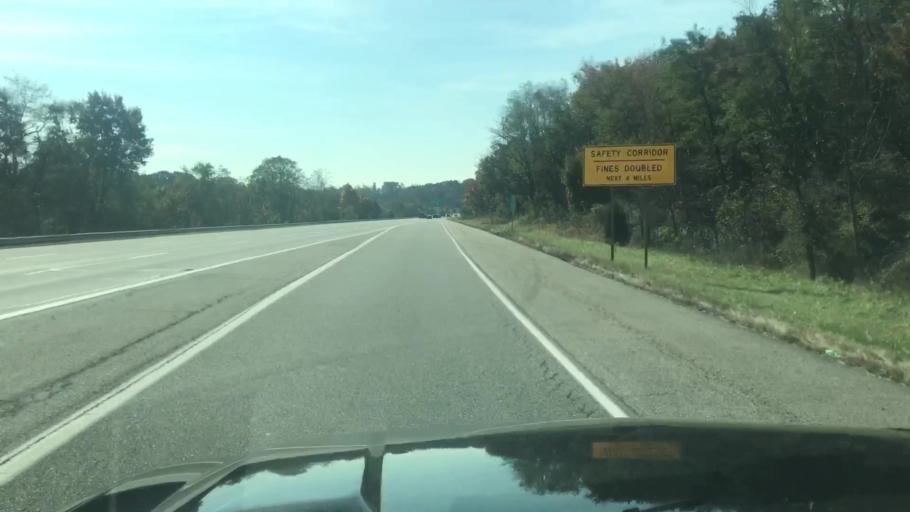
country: US
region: Pennsylvania
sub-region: Cumberland County
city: Enola
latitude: 40.2866
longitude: -76.9830
